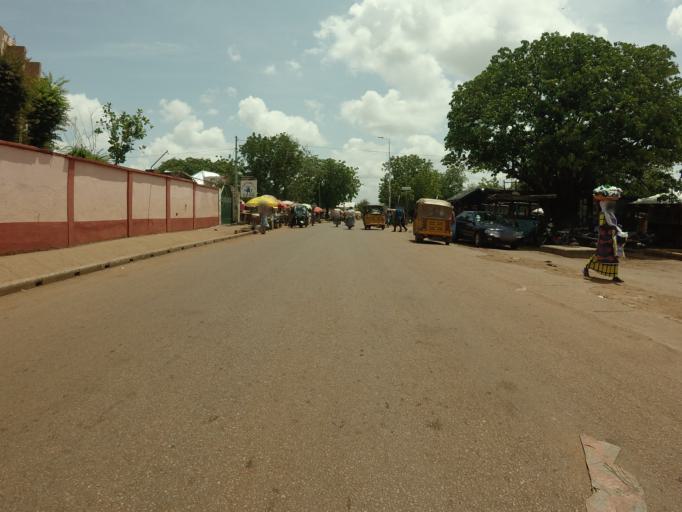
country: GH
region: Northern
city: Tamale
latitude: 9.4013
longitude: -0.8481
